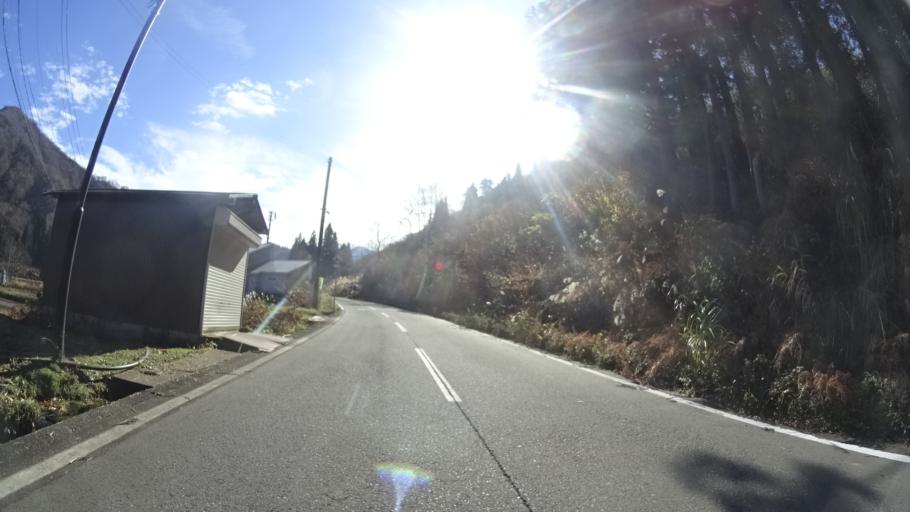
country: JP
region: Niigata
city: Muikamachi
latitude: 37.1915
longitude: 139.0807
